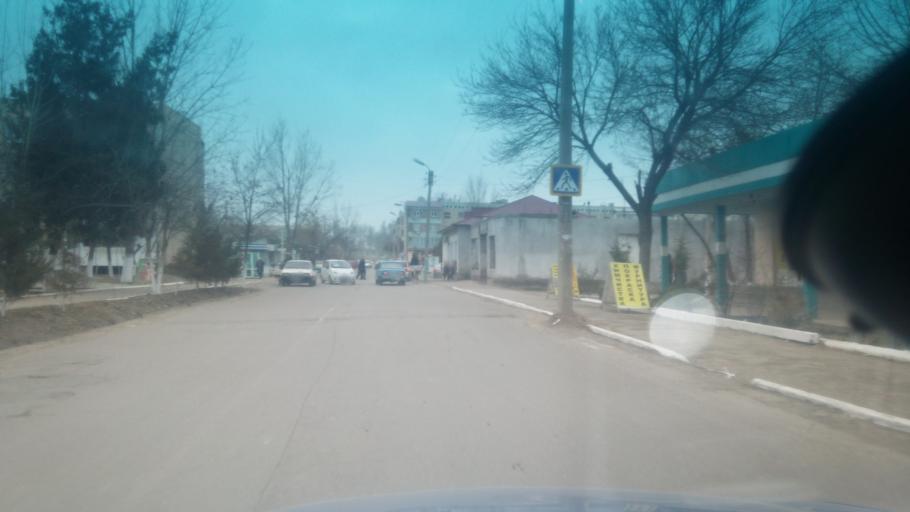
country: UZ
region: Sirdaryo
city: Guliston
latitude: 40.5157
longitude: 68.7795
